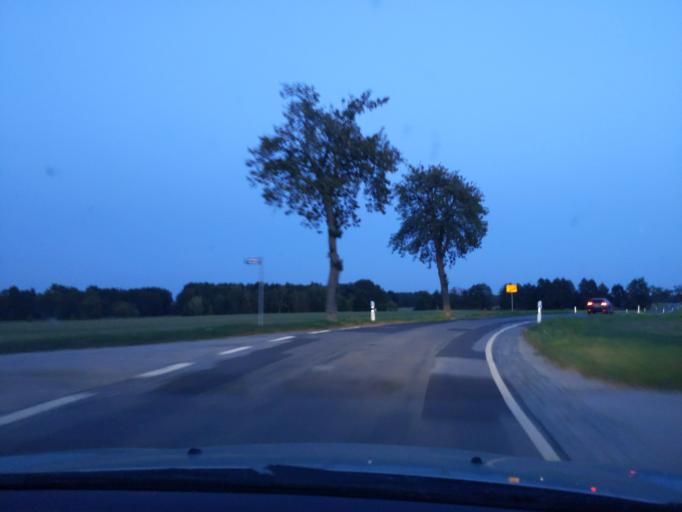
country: DE
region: Saxony
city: Grossdubrau
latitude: 51.2969
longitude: 14.4611
